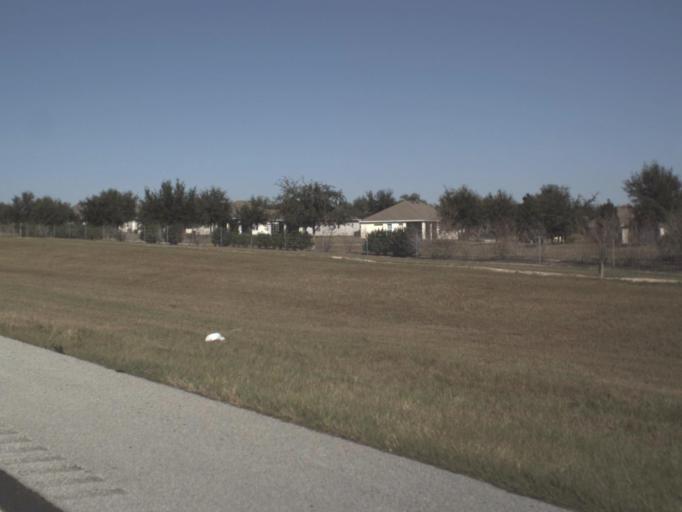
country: US
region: Florida
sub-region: Lake County
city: Hawthorne
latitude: 28.7109
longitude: -81.8917
